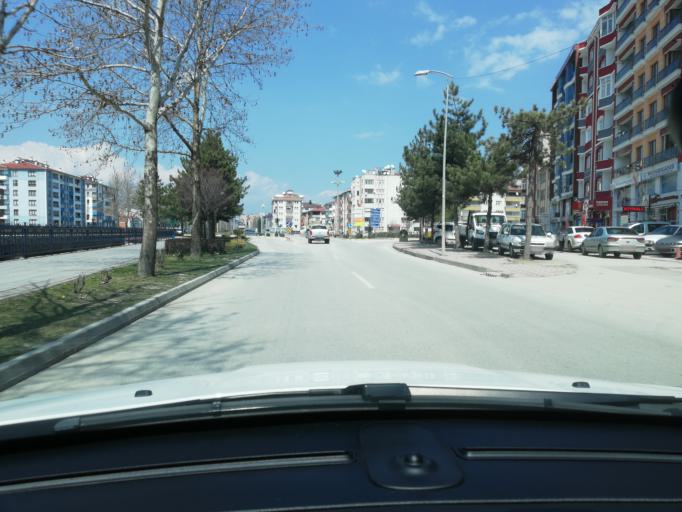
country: TR
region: Kastamonu
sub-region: Cide
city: Kastamonu
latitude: 41.3909
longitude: 33.7817
